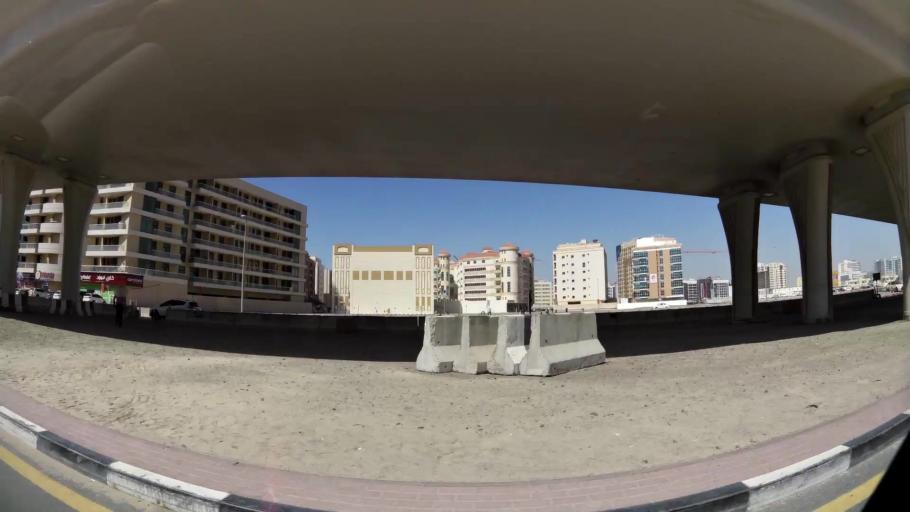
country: AE
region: Dubai
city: Dubai
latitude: 25.1107
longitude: 55.1887
